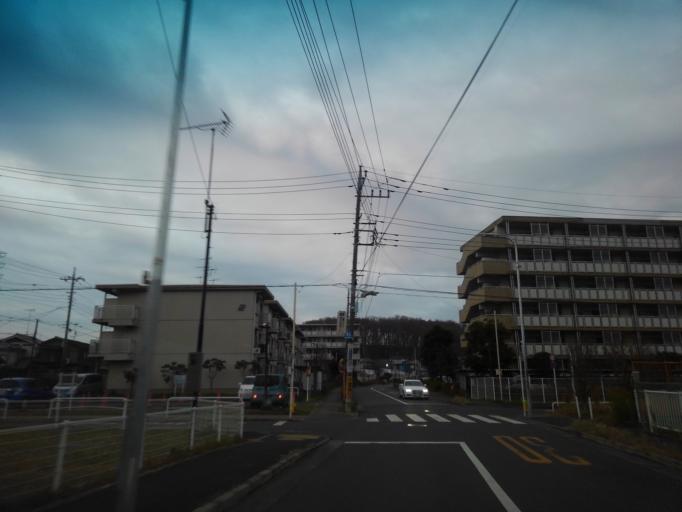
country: JP
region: Tokyo
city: Higashimurayama-shi
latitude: 35.7653
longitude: 139.4508
